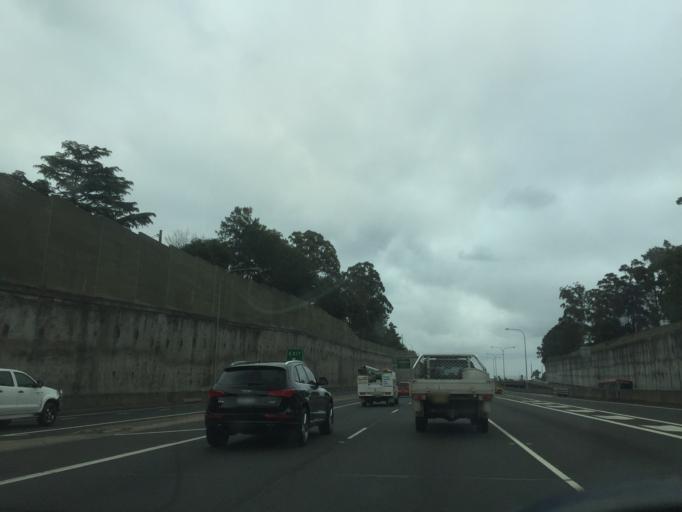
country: AU
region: New South Wales
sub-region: The Hills Shire
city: West Pennant
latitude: -33.7582
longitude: 151.0532
